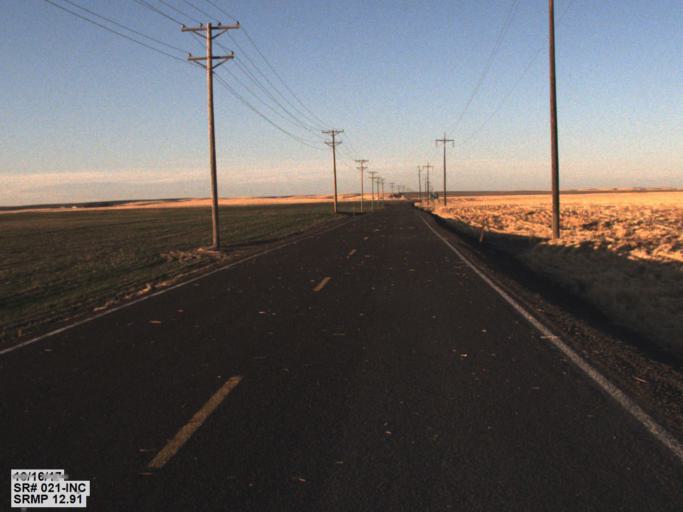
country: US
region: Washington
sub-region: Franklin County
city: Connell
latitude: 46.8132
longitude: -118.5472
